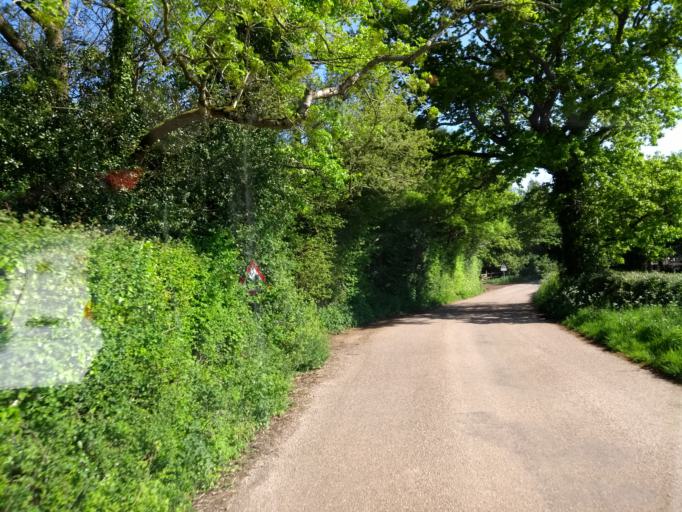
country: GB
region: England
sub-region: Devon
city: Colyton
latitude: 50.7572
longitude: -3.0471
